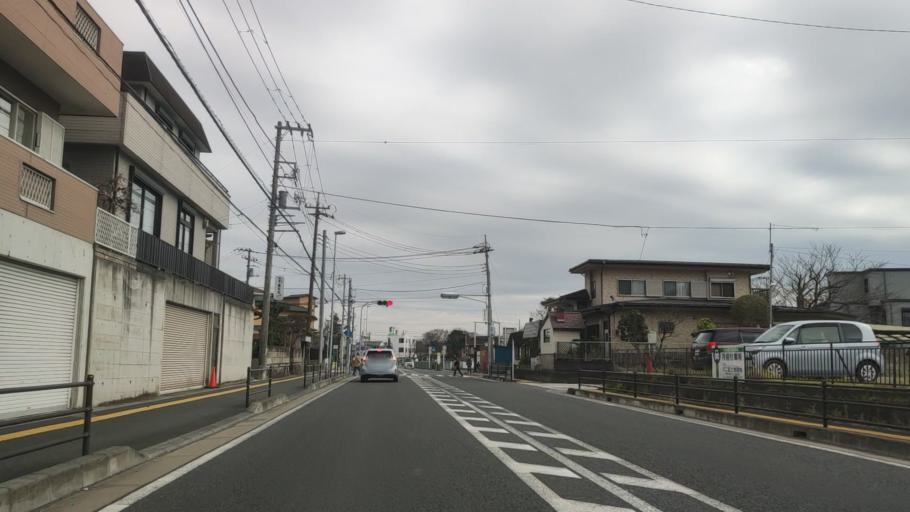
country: JP
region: Kanagawa
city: Ninomiya
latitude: 35.3025
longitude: 139.2579
